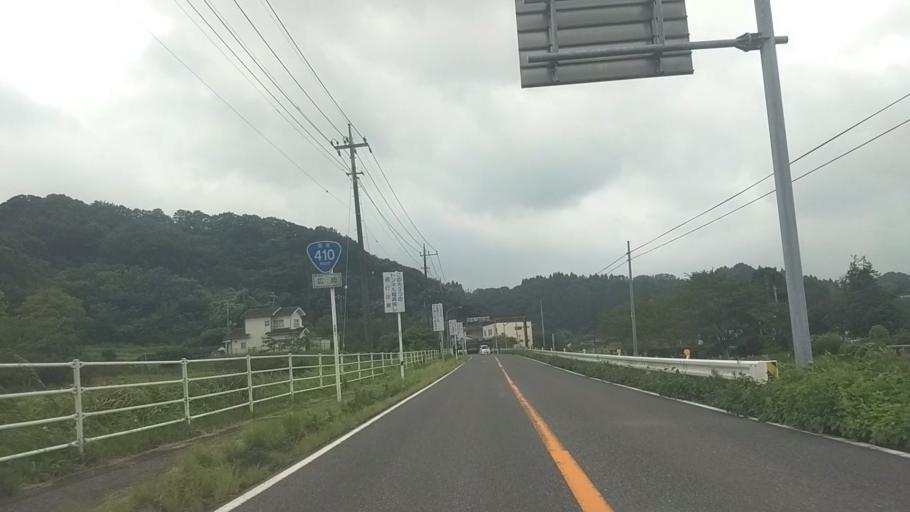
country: JP
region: Chiba
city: Kawaguchi
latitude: 35.2590
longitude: 140.0644
